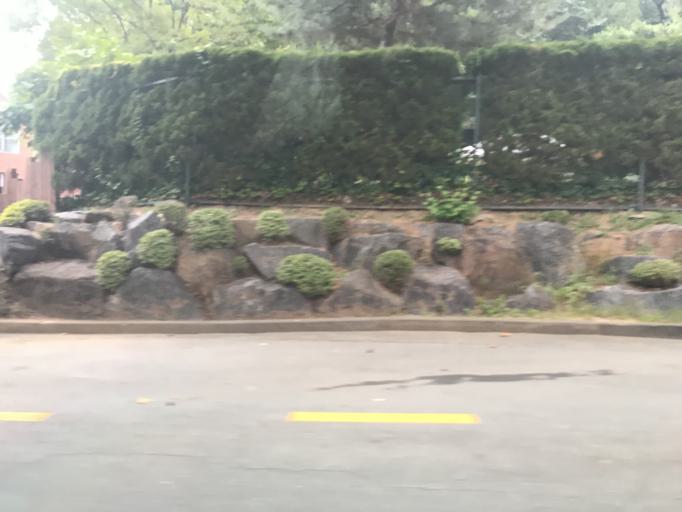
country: KR
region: Seoul
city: Seoul
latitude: 37.5648
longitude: 126.9420
